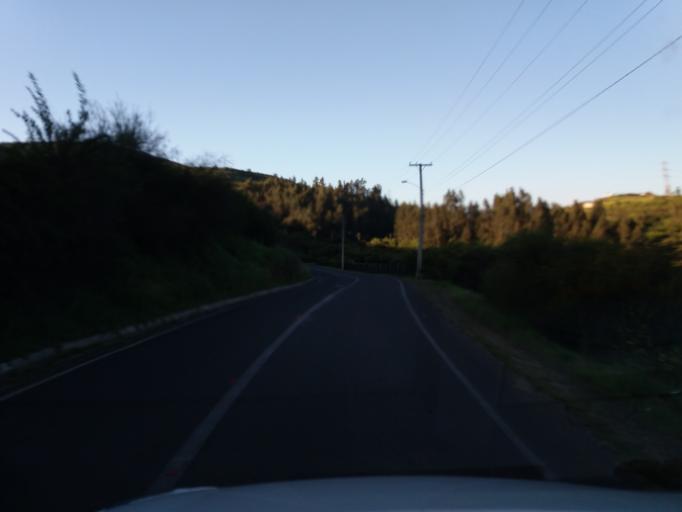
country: CL
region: Valparaiso
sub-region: Provincia de Quillota
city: Quillota
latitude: -32.8894
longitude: -71.2817
